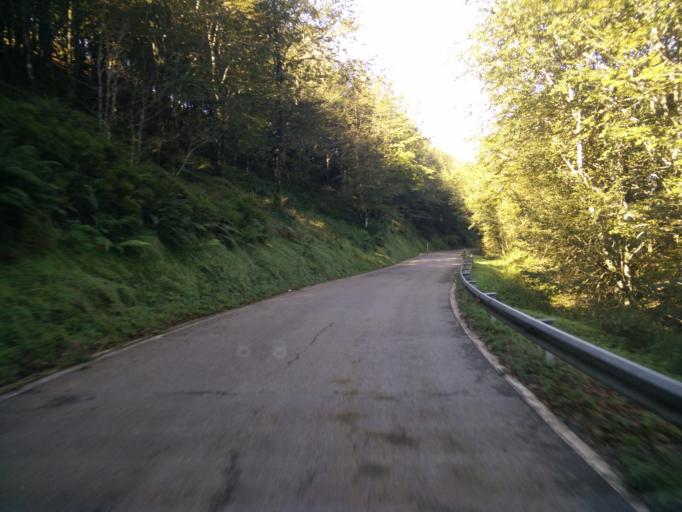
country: ES
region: Cantabria
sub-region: Provincia de Cantabria
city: San Pedro del Romeral
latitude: 43.0519
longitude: -3.8450
